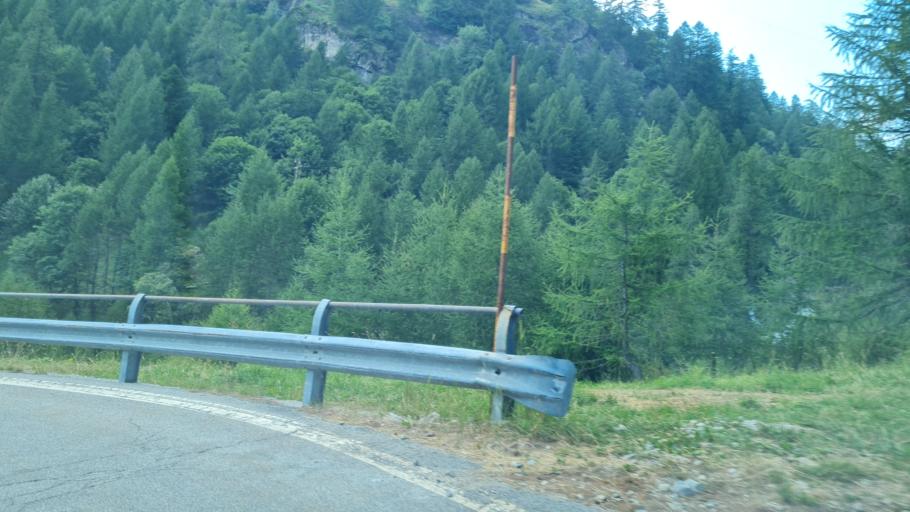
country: IT
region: Piedmont
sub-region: Provincia Verbano-Cusio-Ossola
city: Formazza
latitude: 46.3973
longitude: 8.4197
